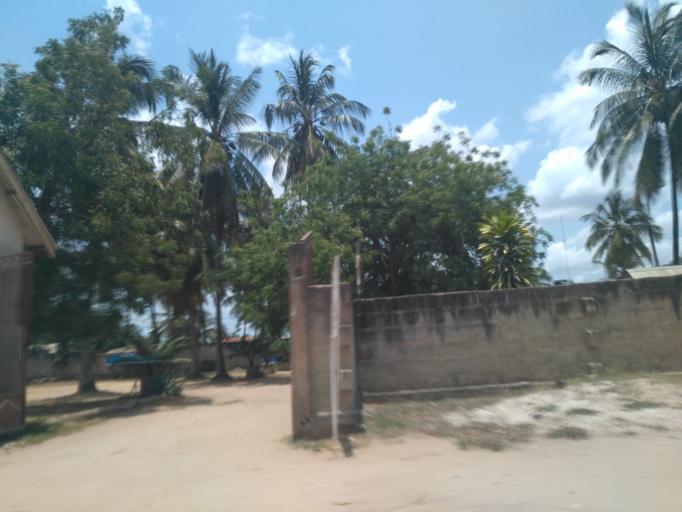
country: TZ
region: Dar es Salaam
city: Dar es Salaam
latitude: -6.8429
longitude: 39.3514
